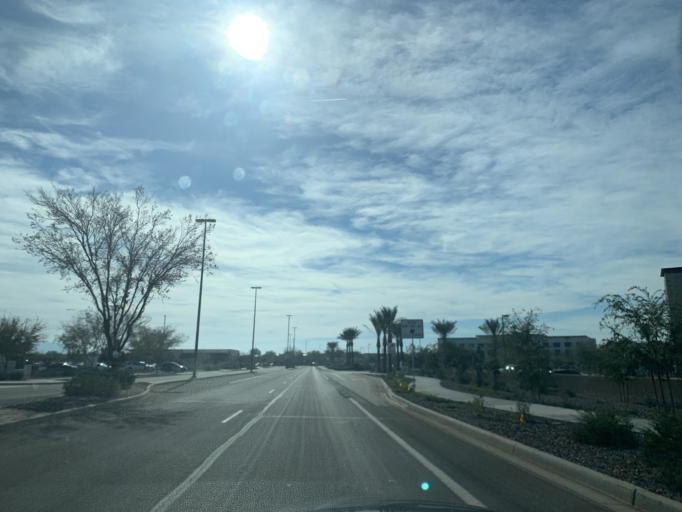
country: US
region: Arizona
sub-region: Maricopa County
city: Gilbert
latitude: 33.2896
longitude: -111.7486
